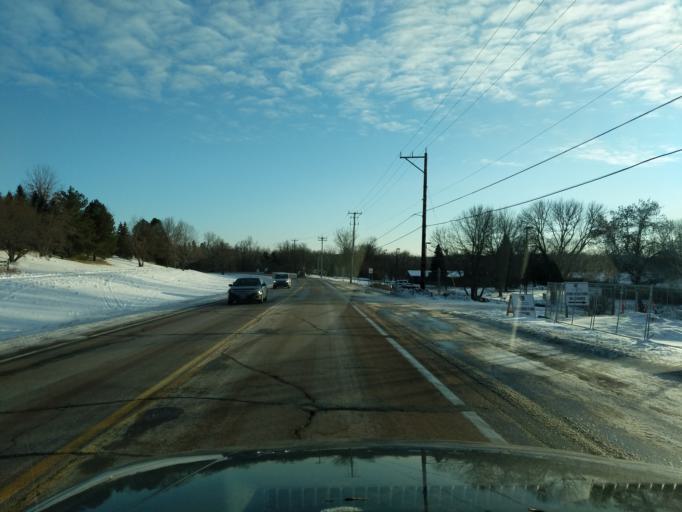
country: US
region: Minnesota
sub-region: Carver County
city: Victoria
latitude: 44.8759
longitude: -93.6413
